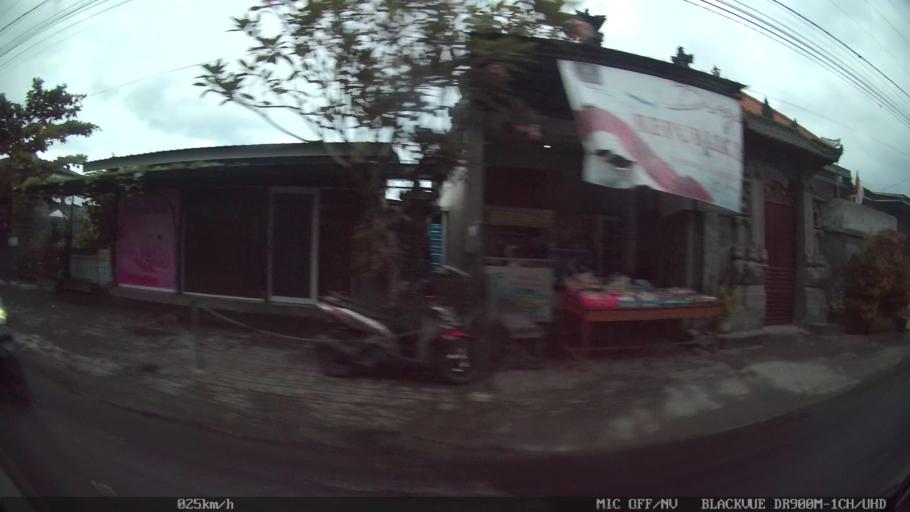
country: ID
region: Bali
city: Banjar Pasekan
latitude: -8.6182
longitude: 115.2671
